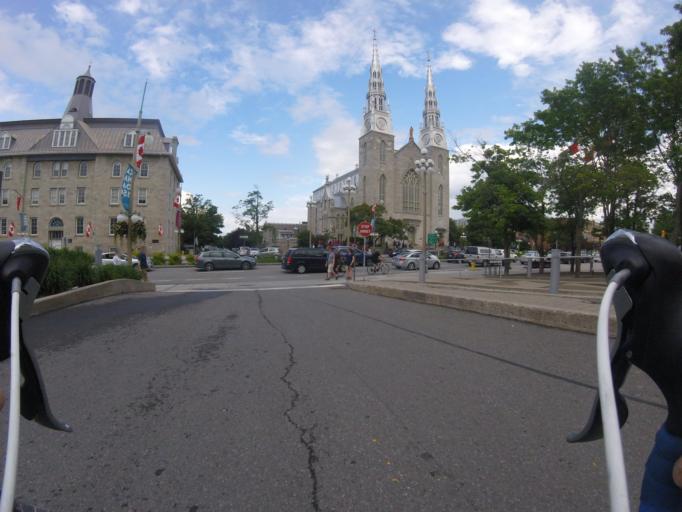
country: CA
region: Ontario
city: Ottawa
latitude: 45.4298
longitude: -75.6976
